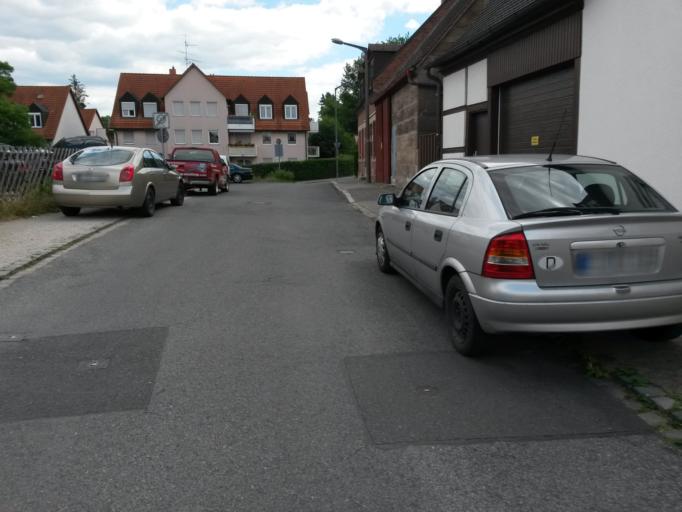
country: DE
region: Bavaria
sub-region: Regierungsbezirk Mittelfranken
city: Furth
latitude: 49.4616
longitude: 10.9722
